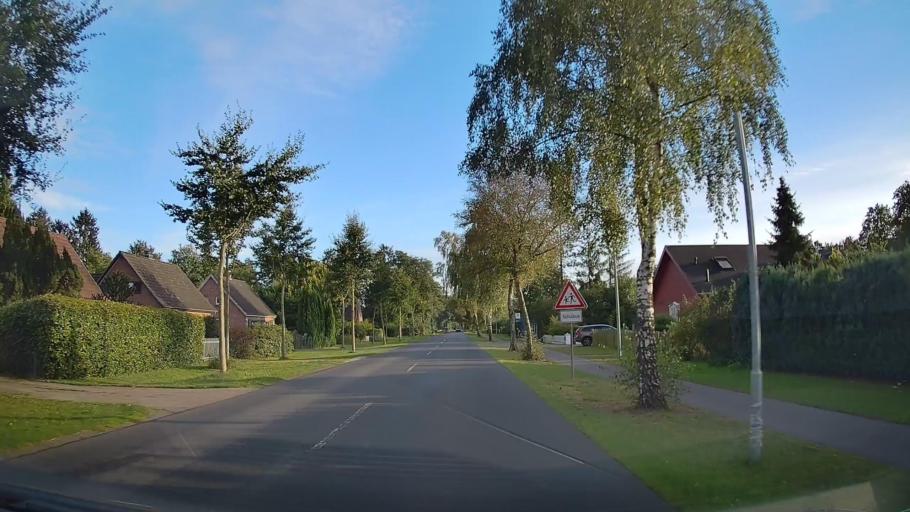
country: DE
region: Lower Saxony
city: Sottrum
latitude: 53.0919
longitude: 9.2362
